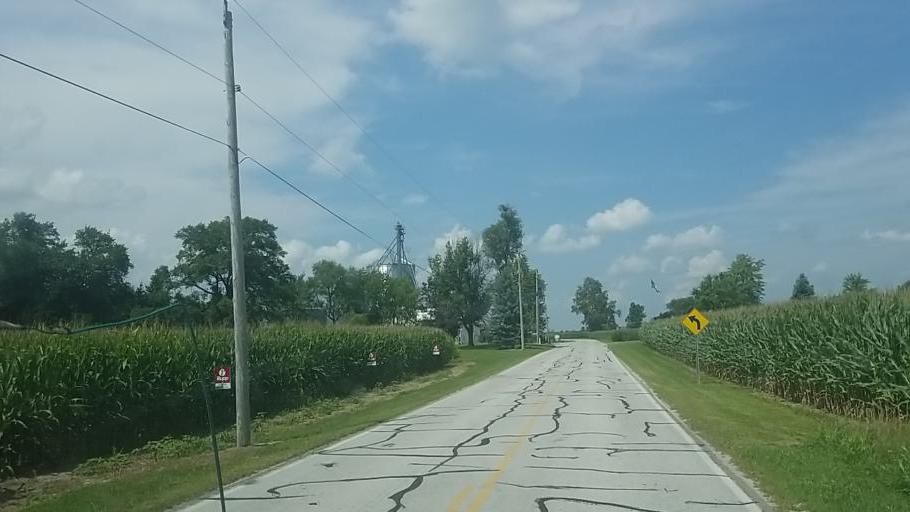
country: US
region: Ohio
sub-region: Hardin County
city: Kenton
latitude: 40.6898
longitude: -83.5738
